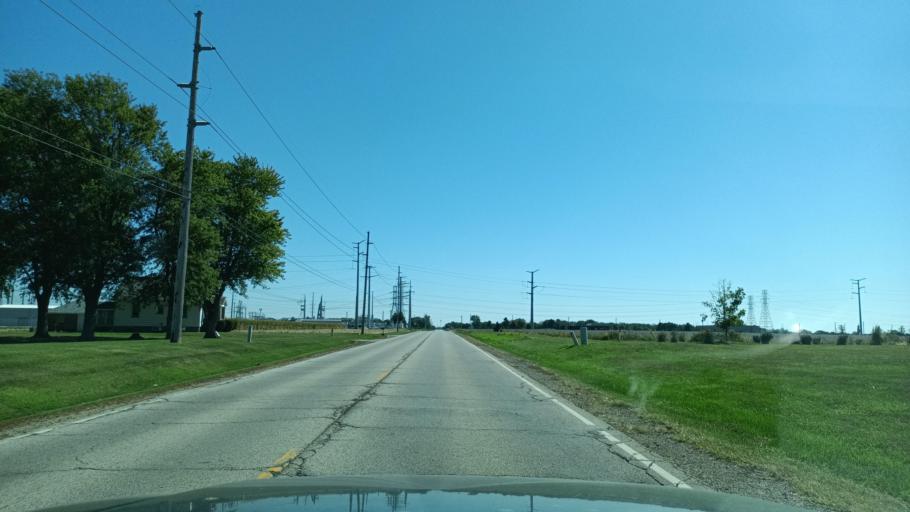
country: US
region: Illinois
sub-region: Peoria County
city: Dunlap
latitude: 40.7824
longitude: -89.7044
